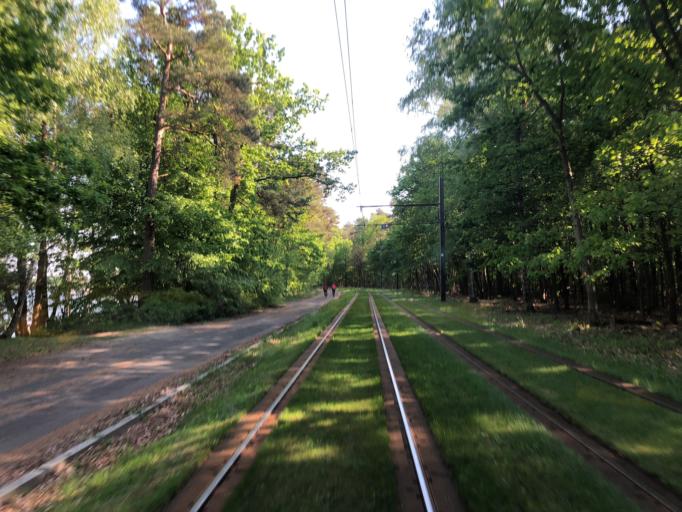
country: DE
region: Brandenburg
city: Zeuthen
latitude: 52.4040
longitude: 13.6233
